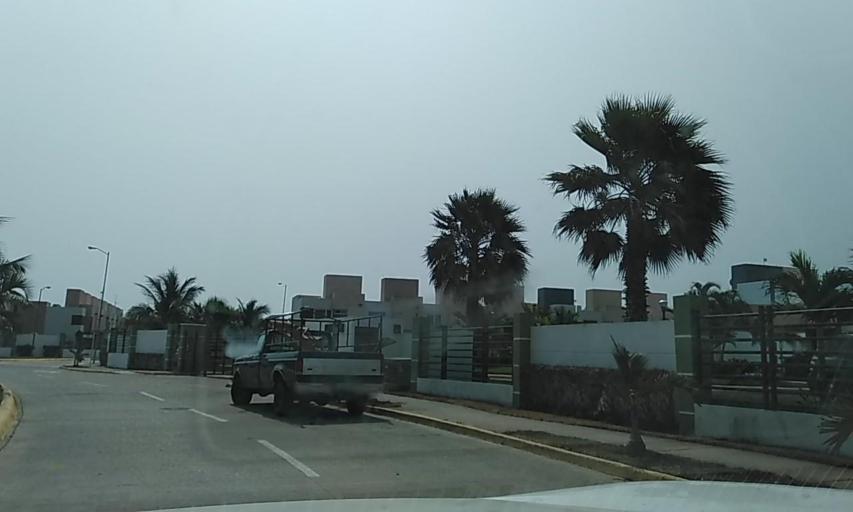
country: MX
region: Veracruz
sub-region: Veracruz
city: Hacienda Sotavento
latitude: 19.1300
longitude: -96.1684
